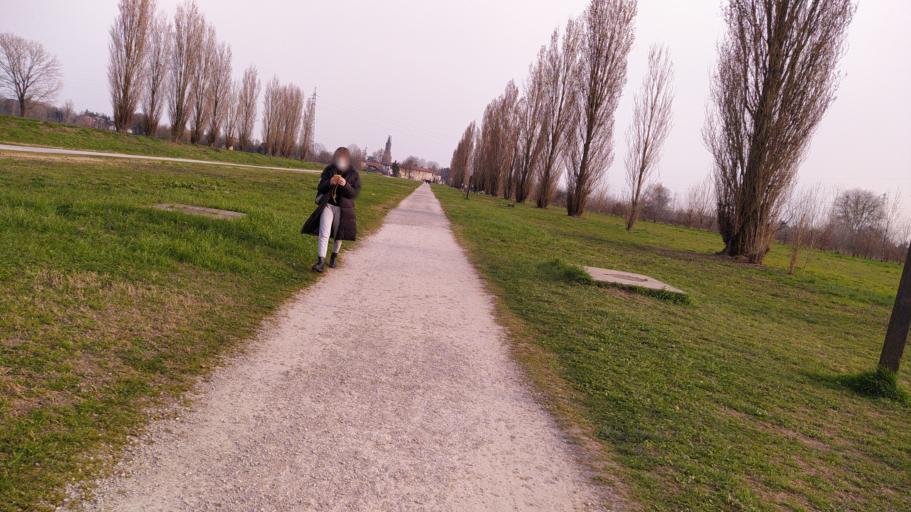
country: IT
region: Lombardy
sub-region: Citta metropolitana di Milano
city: Chiaravalle
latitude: 45.4223
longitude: 9.2294
